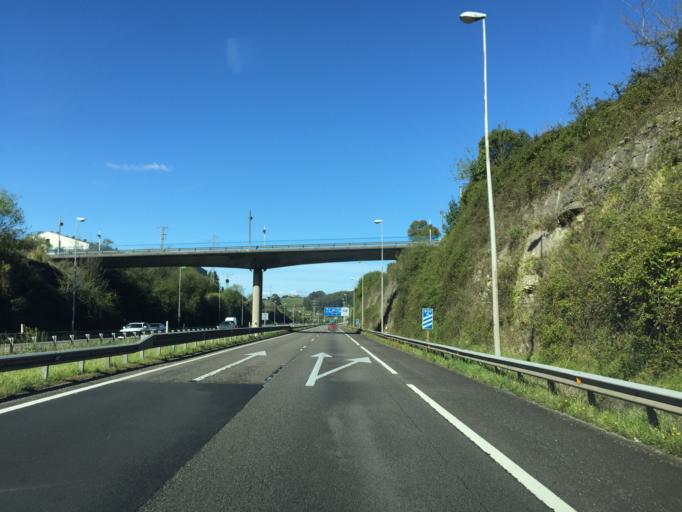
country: ES
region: Asturias
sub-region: Province of Asturias
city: Natahoyo
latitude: 43.5131
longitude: -5.6776
